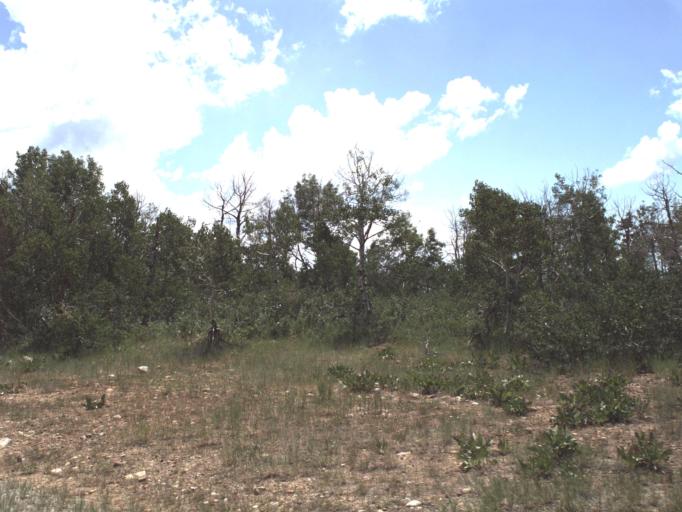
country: US
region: Utah
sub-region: Weber County
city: Wolf Creek
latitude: 41.4103
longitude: -111.5583
